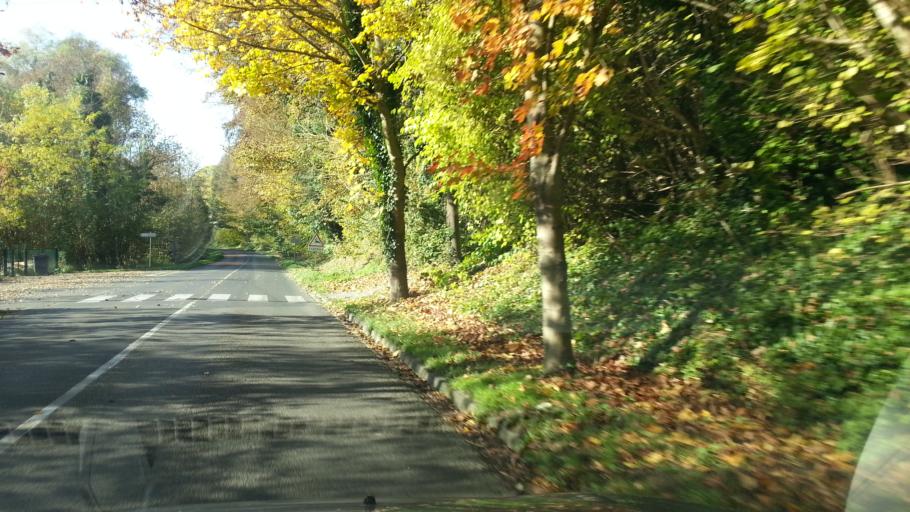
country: FR
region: Picardie
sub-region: Departement de l'Oise
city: Cires-les-Mello
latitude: 49.2659
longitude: 2.3893
